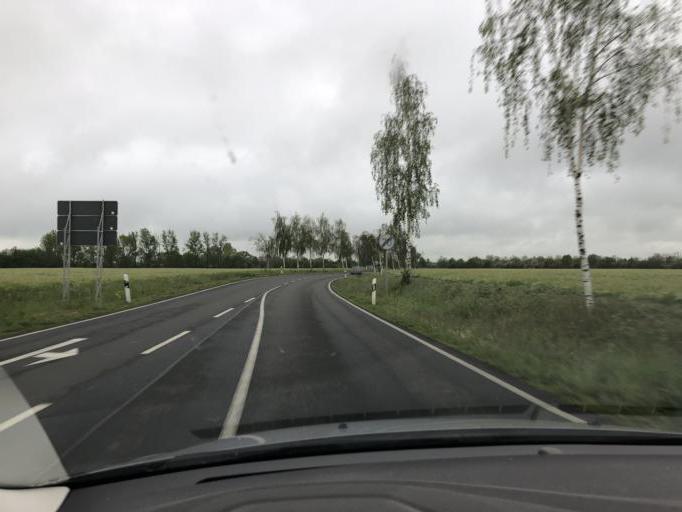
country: DE
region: Saxony
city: Dobernitz
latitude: 51.5249
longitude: 12.3684
